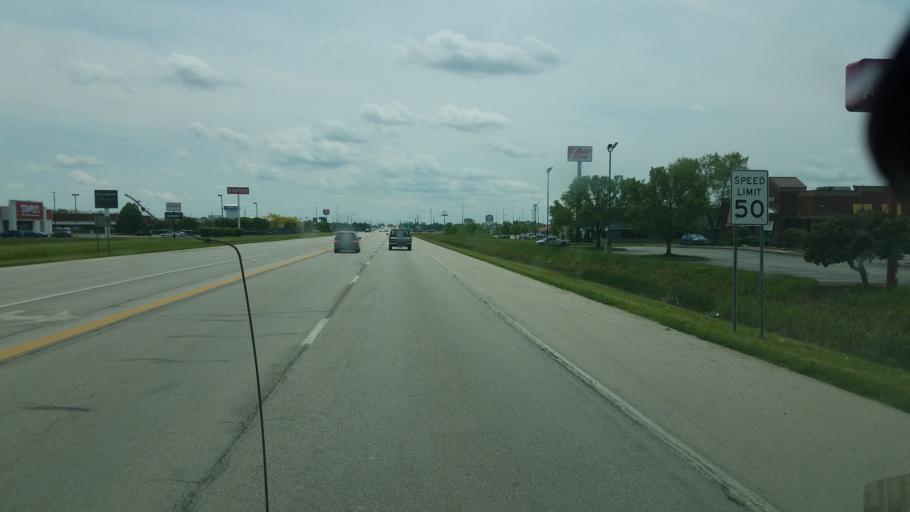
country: US
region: Ohio
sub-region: Sandusky County
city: Fremont
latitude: 41.3771
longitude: -83.1175
